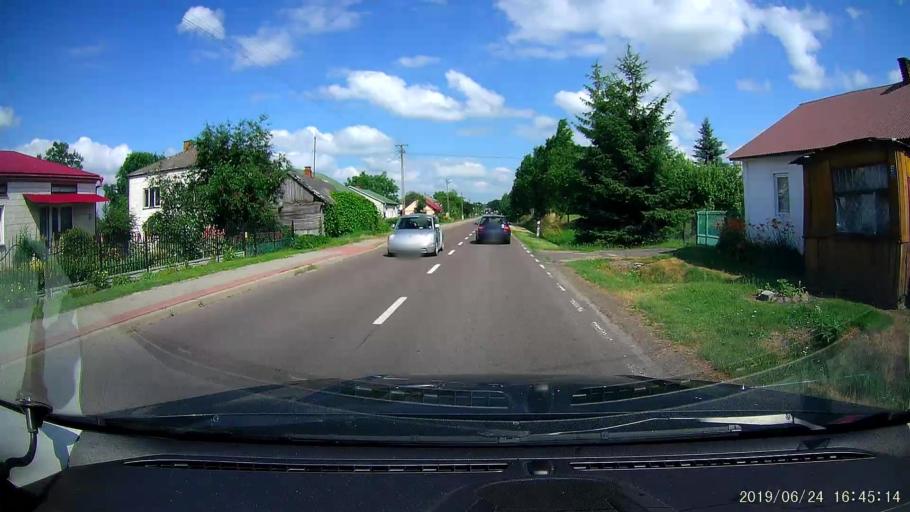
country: PL
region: Lublin Voivodeship
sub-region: Powiat tomaszowski
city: Laszczow
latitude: 50.5327
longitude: 23.6652
